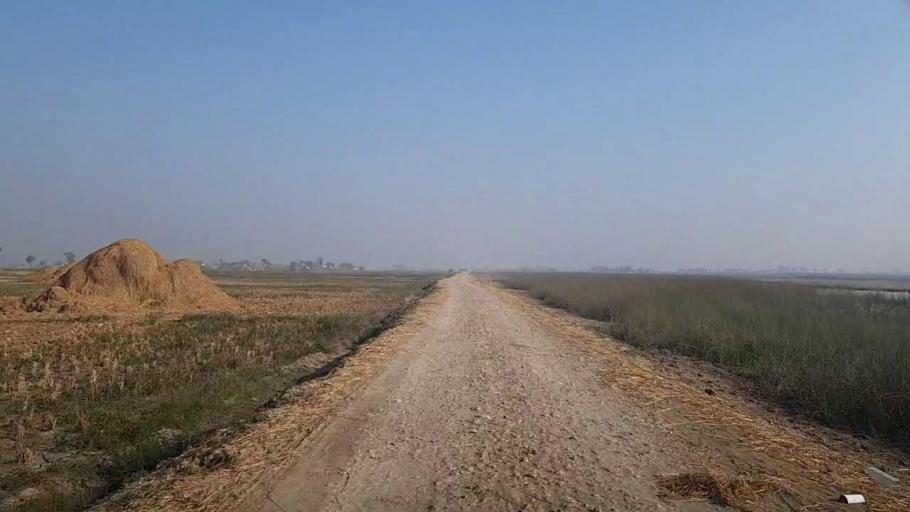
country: PK
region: Sindh
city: Radhan
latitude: 27.1386
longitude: 67.9067
